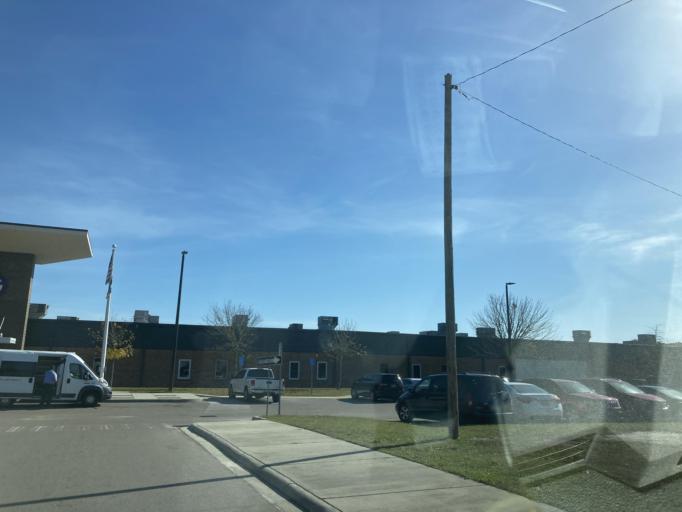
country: US
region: Mississippi
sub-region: Harrison County
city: West Gulfport
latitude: 30.3902
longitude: -89.0432
